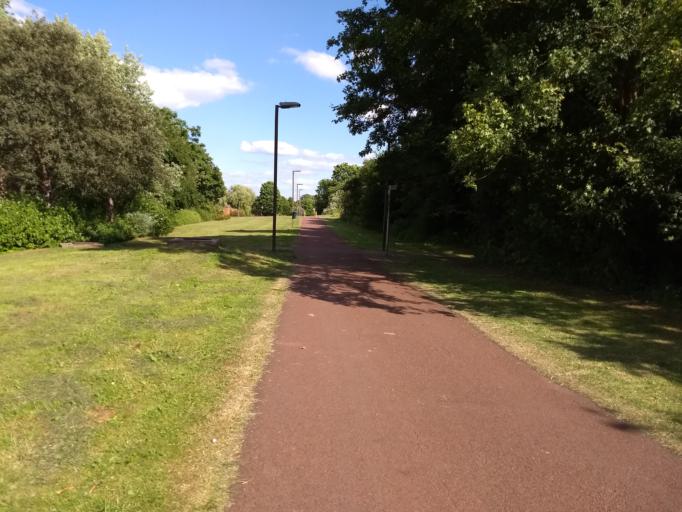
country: GB
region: England
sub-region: Milton Keynes
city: Shenley Church End
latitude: 52.0318
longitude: -0.7975
